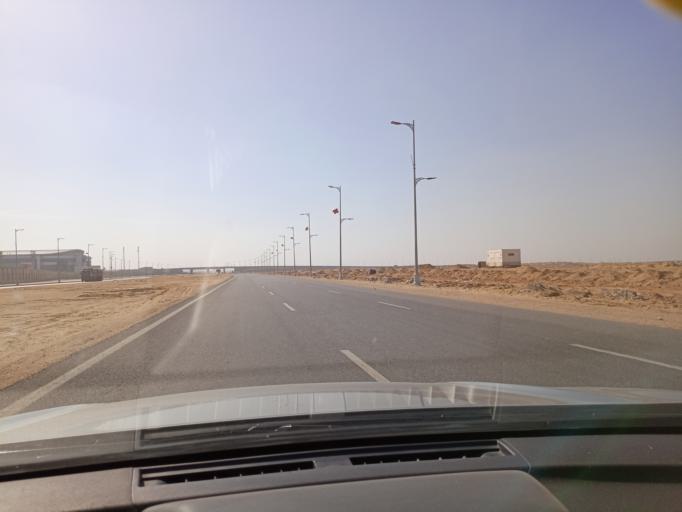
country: EG
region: Muhafazat al Qalyubiyah
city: Al Khankah
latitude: 30.0444
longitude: 31.6948
